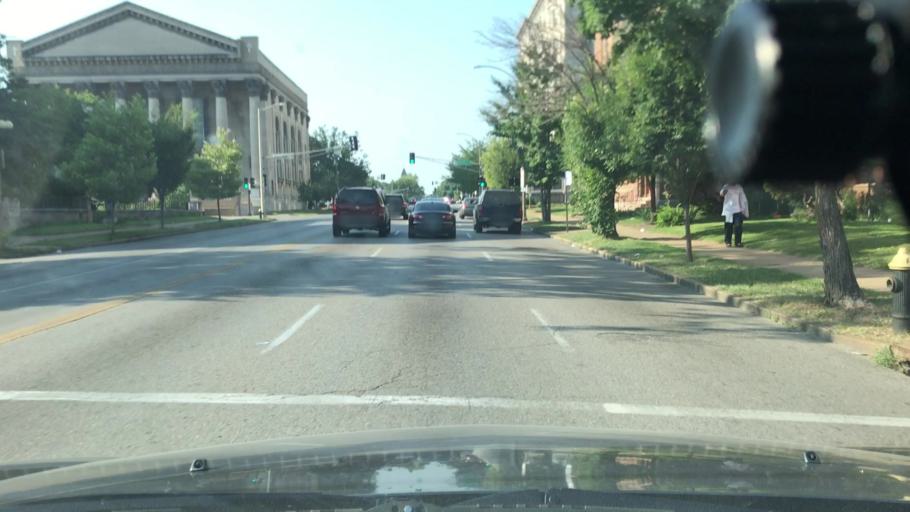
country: US
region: Missouri
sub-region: Saint Louis County
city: Hillsdale
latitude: 38.6497
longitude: -90.2638
